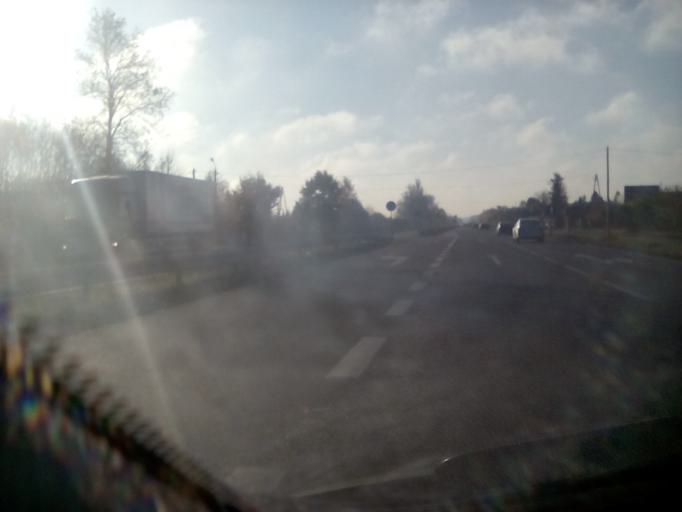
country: PL
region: Masovian Voivodeship
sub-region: Powiat piaseczynski
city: Tarczyn
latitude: 51.9322
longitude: 20.8486
